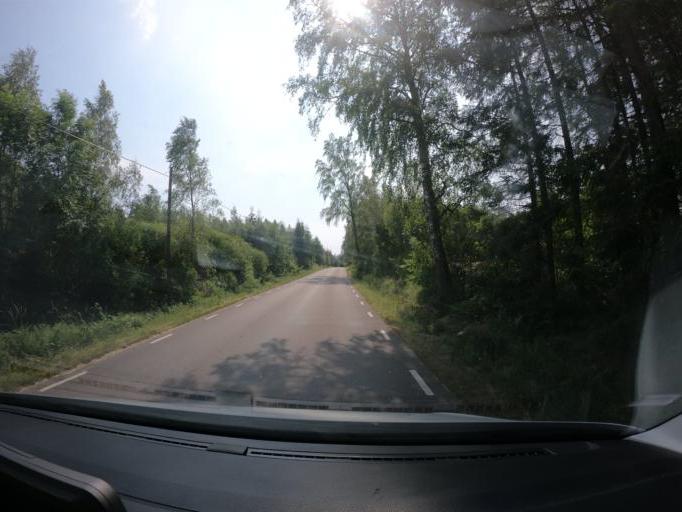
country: SE
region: Skane
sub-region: Hassleholms Kommun
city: Bjarnum
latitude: 56.3327
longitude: 13.6225
